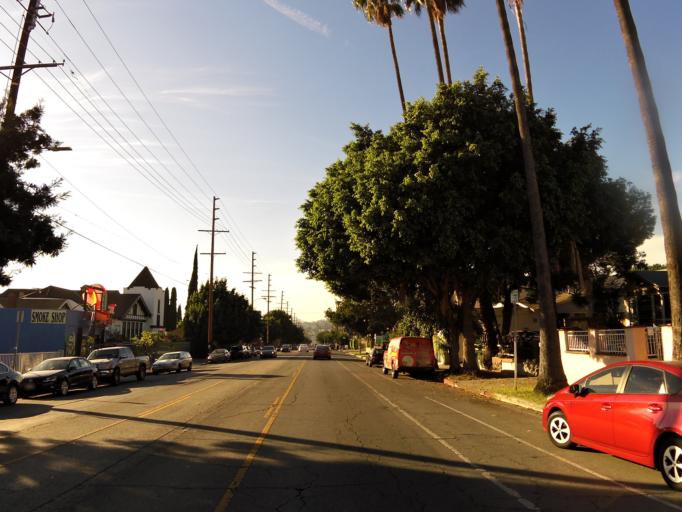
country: US
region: California
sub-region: Los Angeles County
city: Glendale
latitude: 34.1217
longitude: -118.2079
